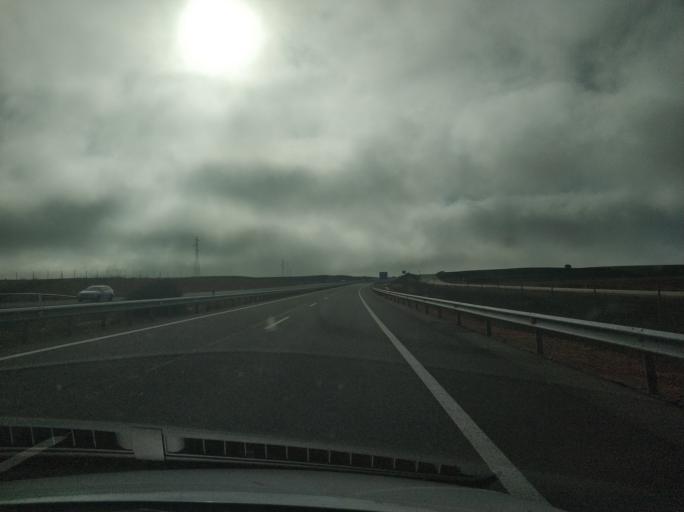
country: ES
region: Castille and Leon
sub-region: Provincia de Soria
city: Alcubilla de las Penas
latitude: 41.2786
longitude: -2.4753
